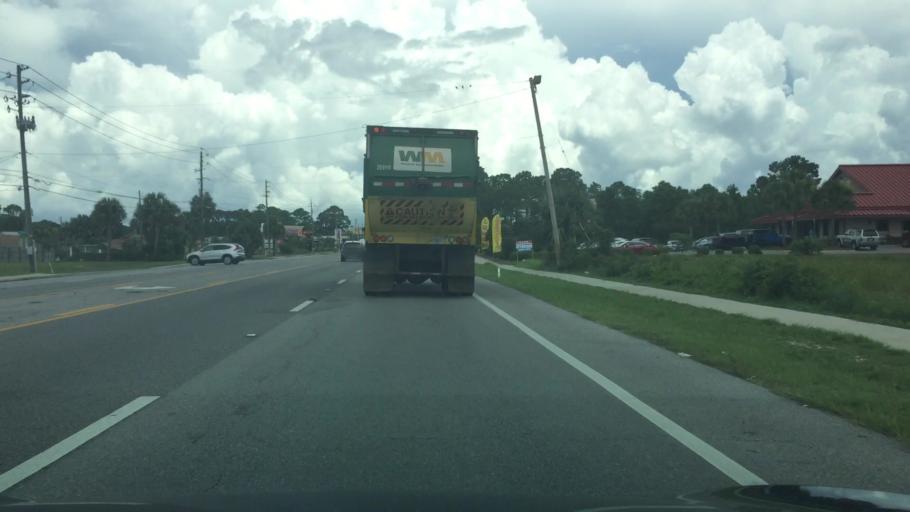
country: US
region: Florida
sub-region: Bay County
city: Lower Grand Lagoon
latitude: 30.1554
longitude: -85.7515
